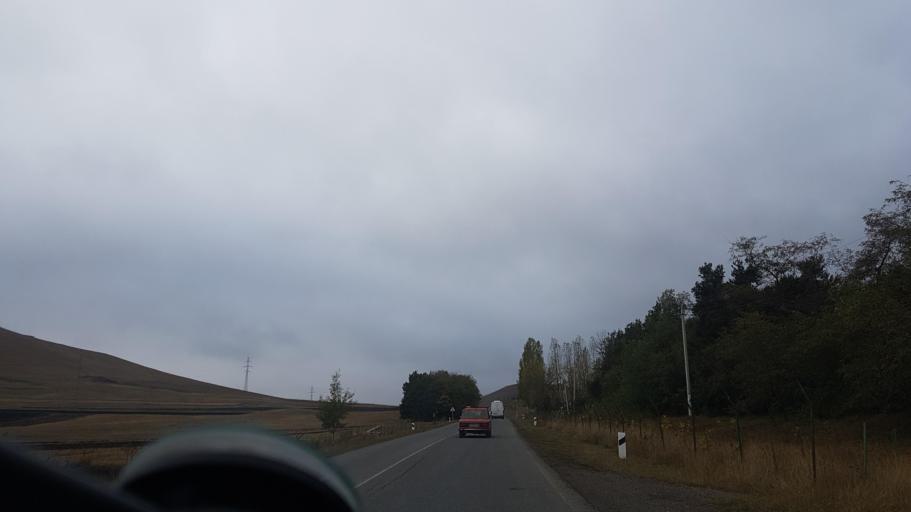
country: AZ
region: Gadabay Rayon
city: Ariqdam
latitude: 40.6245
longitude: 45.8156
